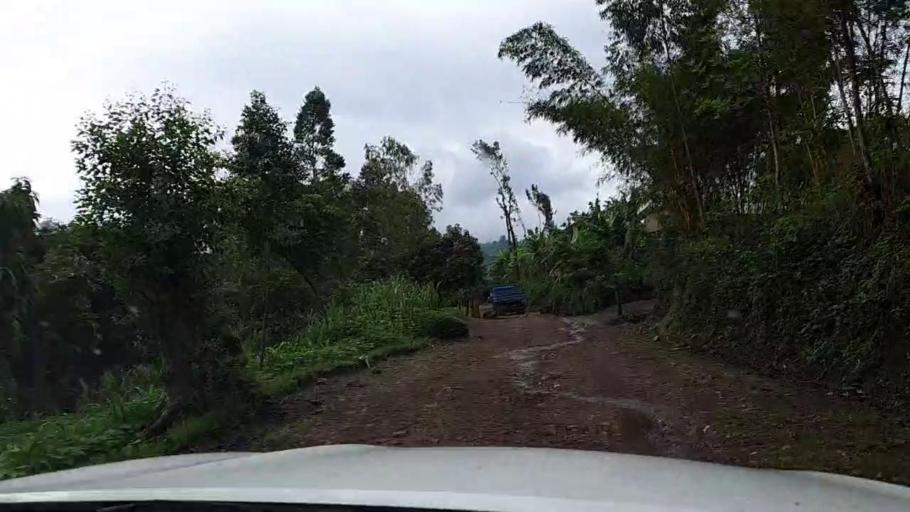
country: RW
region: Western Province
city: Cyangugu
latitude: -2.5486
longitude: 29.0383
